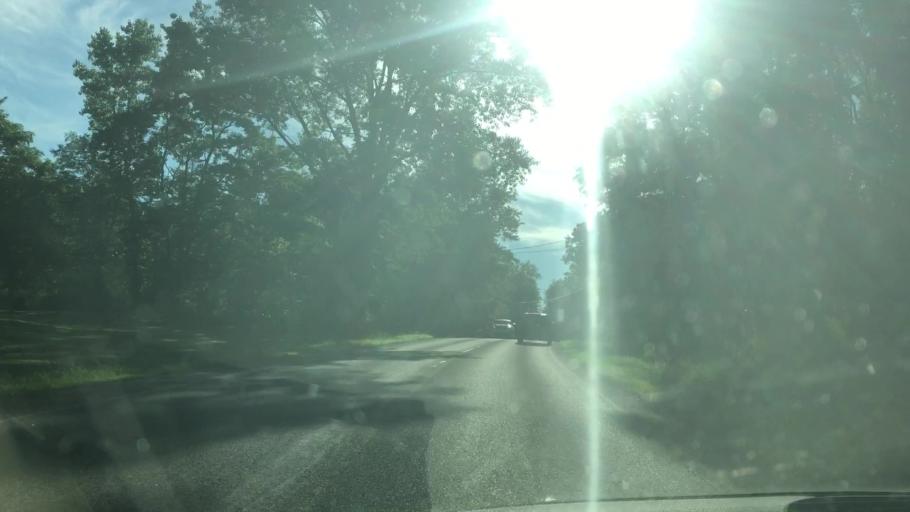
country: US
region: New York
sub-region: Wayne County
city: Macedon
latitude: 43.0437
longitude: -77.3437
